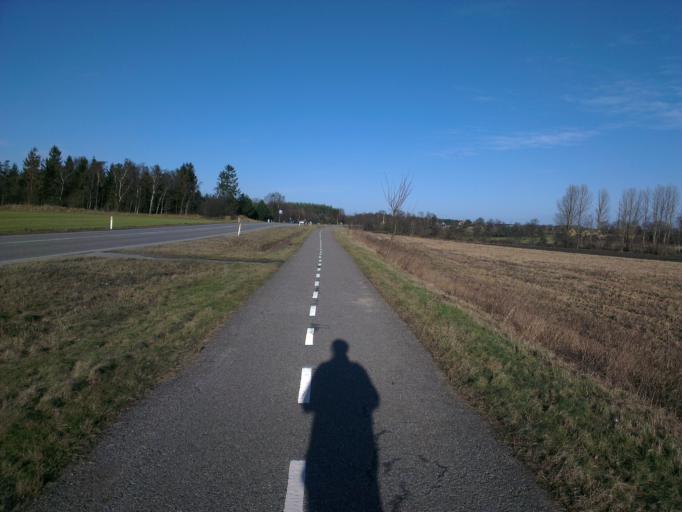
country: DK
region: Capital Region
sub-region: Frederikssund Kommune
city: Jaegerspris
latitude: 55.8134
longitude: 11.9953
